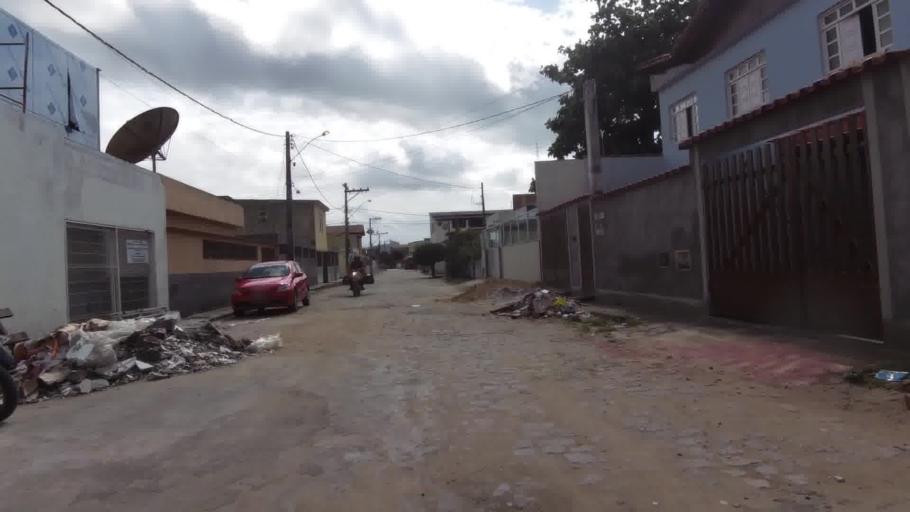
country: BR
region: Espirito Santo
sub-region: Marataizes
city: Marataizes
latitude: -21.0360
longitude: -40.8205
